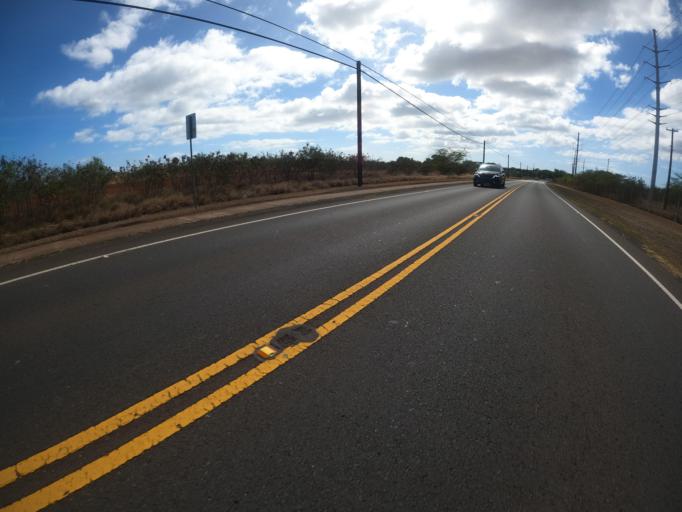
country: US
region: Hawaii
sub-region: Honolulu County
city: Makakilo City
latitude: 21.3235
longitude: -158.0715
